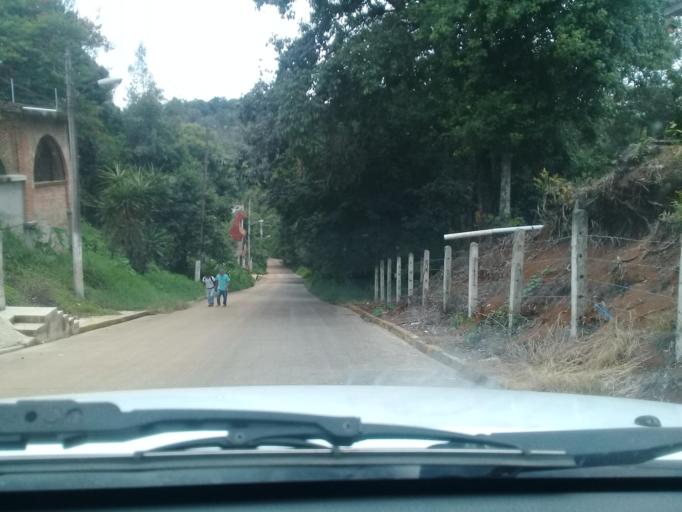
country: MX
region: Veracruz
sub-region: Xalapa
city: Xalapa de Enriquez
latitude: 19.5066
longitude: -96.9138
